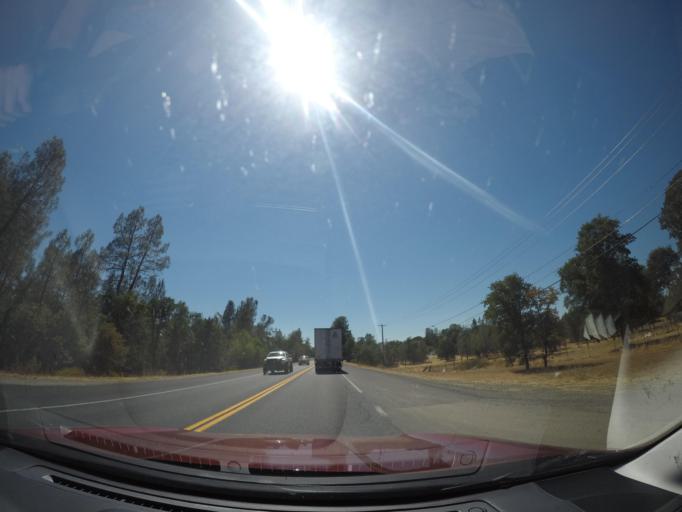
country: US
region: California
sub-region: Shasta County
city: Bella Vista
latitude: 40.6276
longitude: -122.2874
